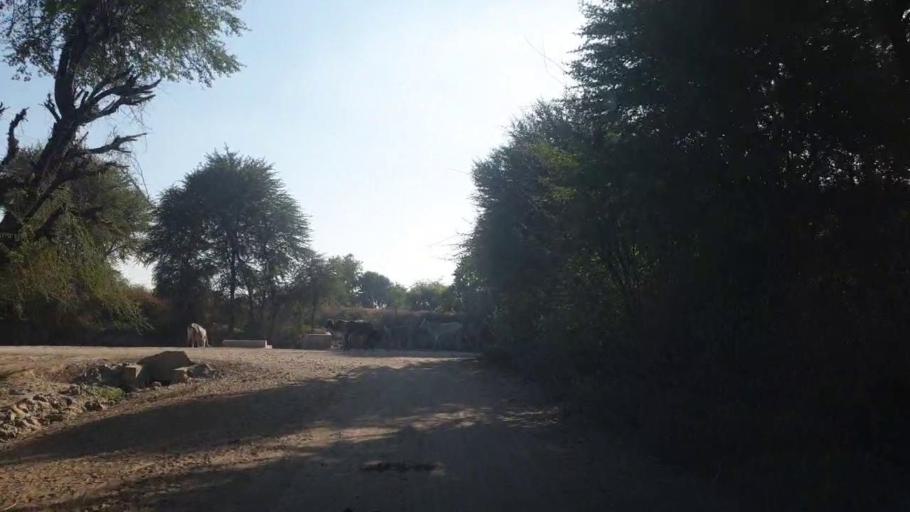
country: PK
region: Sindh
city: Mirwah Gorchani
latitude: 25.4220
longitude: 69.1637
